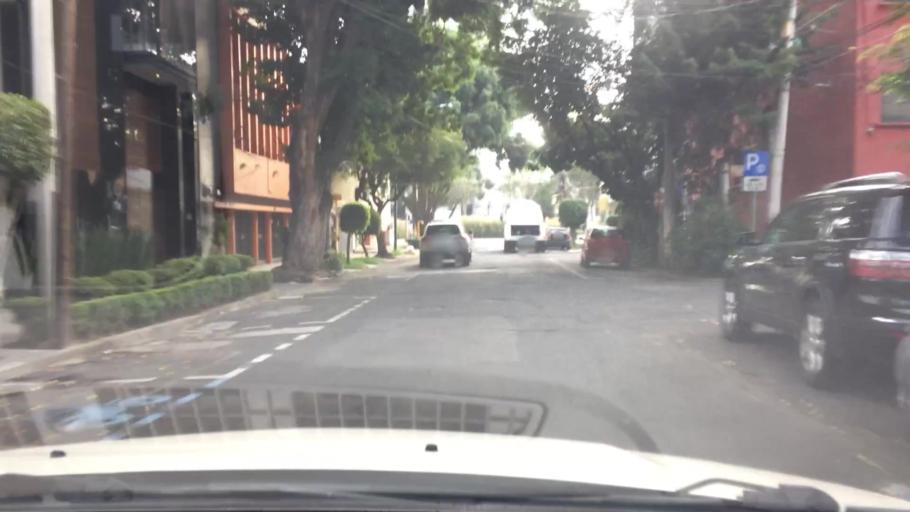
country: MX
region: Mexico City
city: Alvaro Obregon
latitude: 19.3658
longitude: -99.1797
